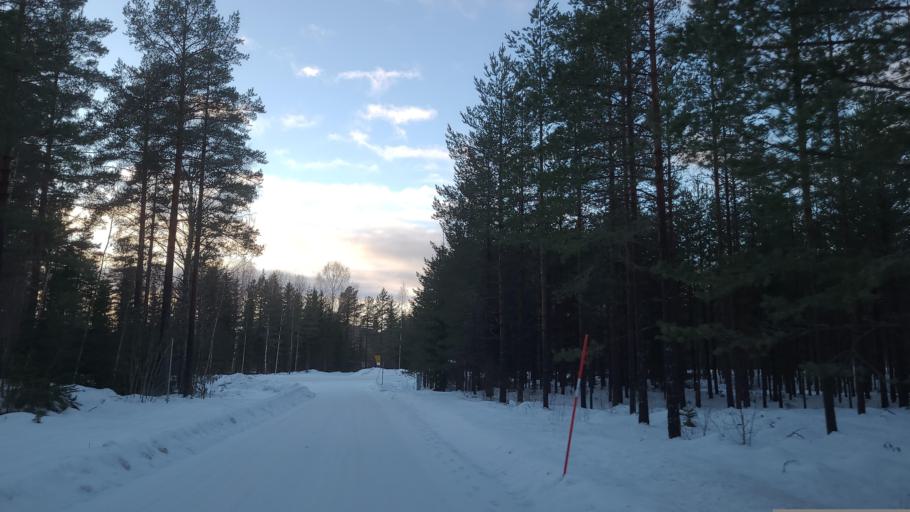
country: SE
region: Gaevleborg
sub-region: Bollnas Kommun
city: Kilafors
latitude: 61.3648
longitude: 16.6612
